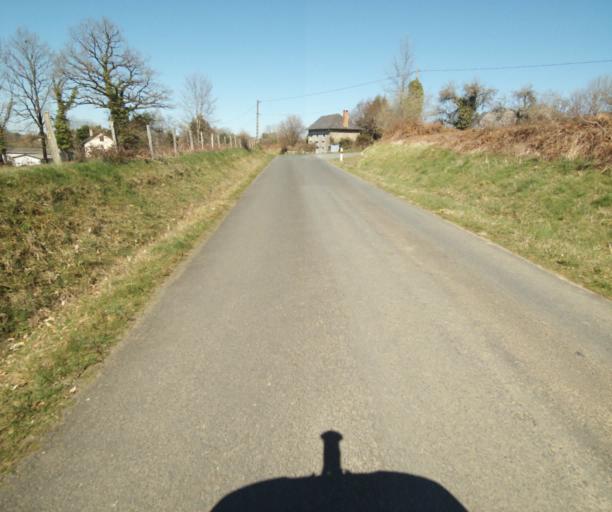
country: FR
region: Limousin
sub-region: Departement de la Correze
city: Saint-Clement
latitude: 45.3359
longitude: 1.6537
